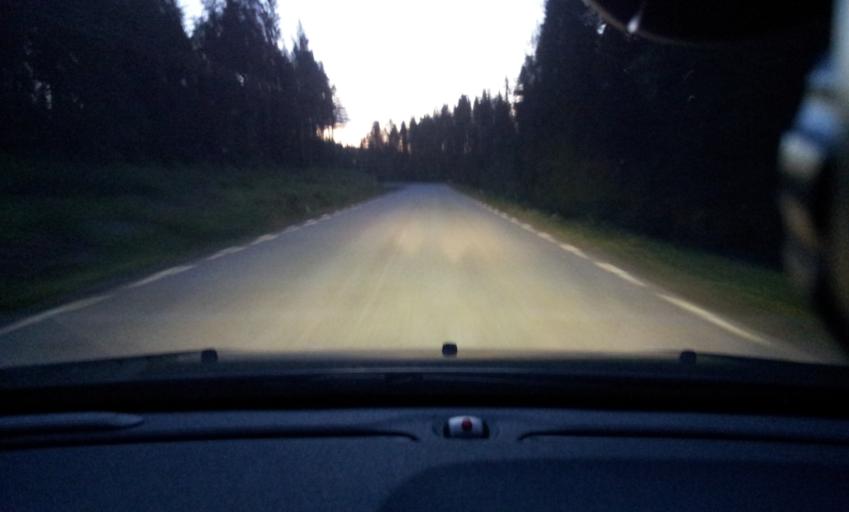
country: SE
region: Jaemtland
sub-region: Bergs Kommun
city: Hoverberg
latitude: 62.7161
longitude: 14.6074
